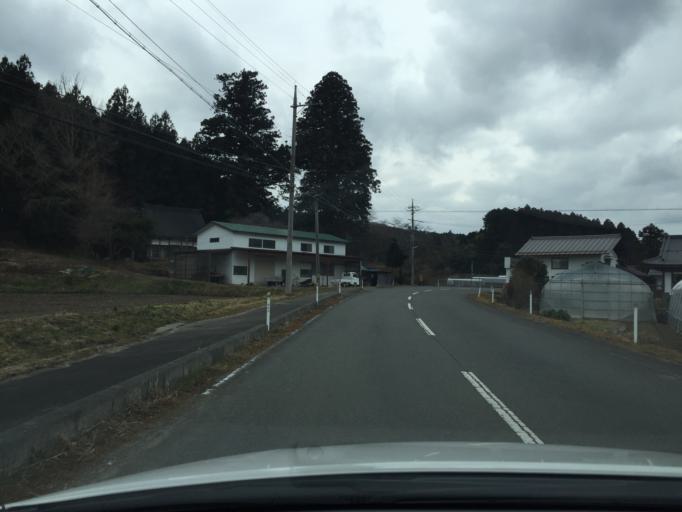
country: JP
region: Fukushima
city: Iwaki
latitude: 37.1799
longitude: 140.7197
